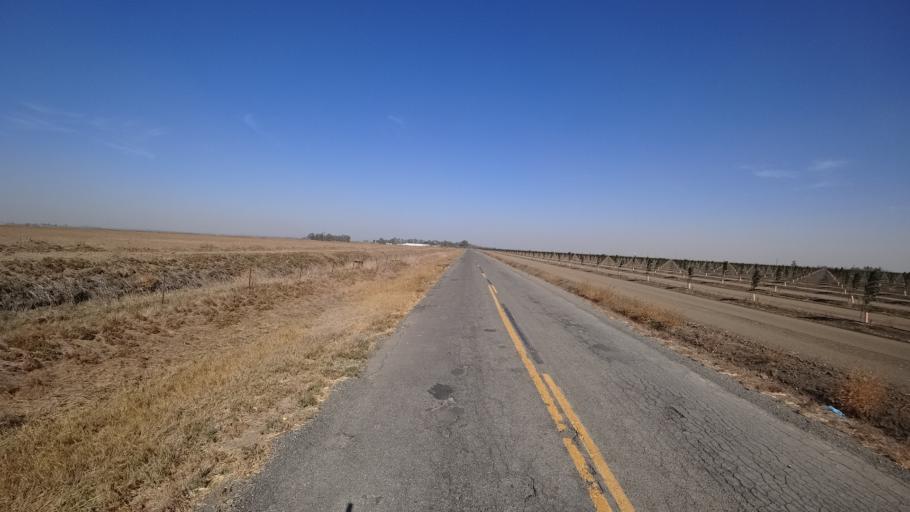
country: US
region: California
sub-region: Yolo County
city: Davis
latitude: 38.4753
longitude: -121.6937
